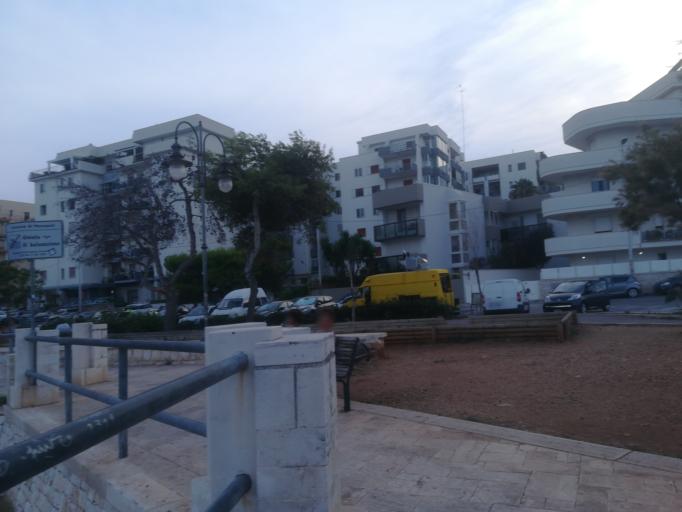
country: IT
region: Apulia
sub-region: Provincia di Bari
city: Monopoli
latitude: 40.9491
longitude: 17.3064
